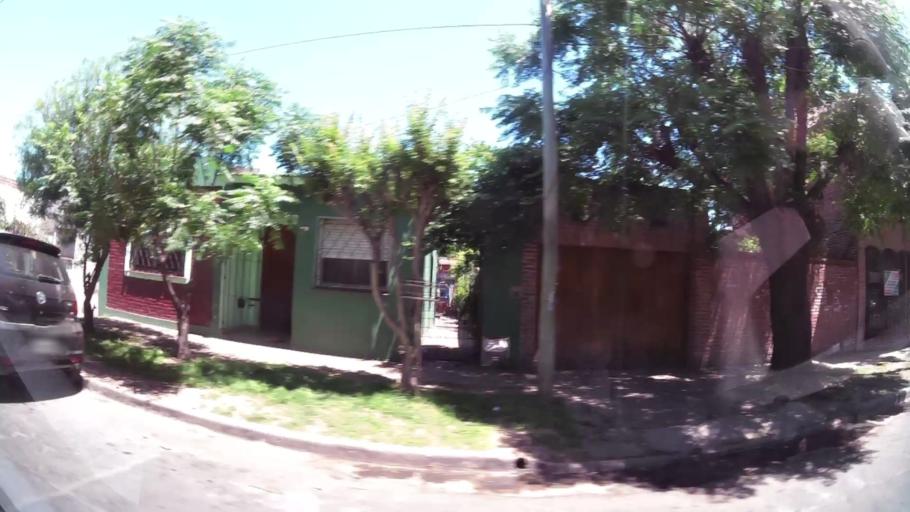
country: AR
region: Buenos Aires
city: Hurlingham
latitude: -34.4991
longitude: -58.6972
